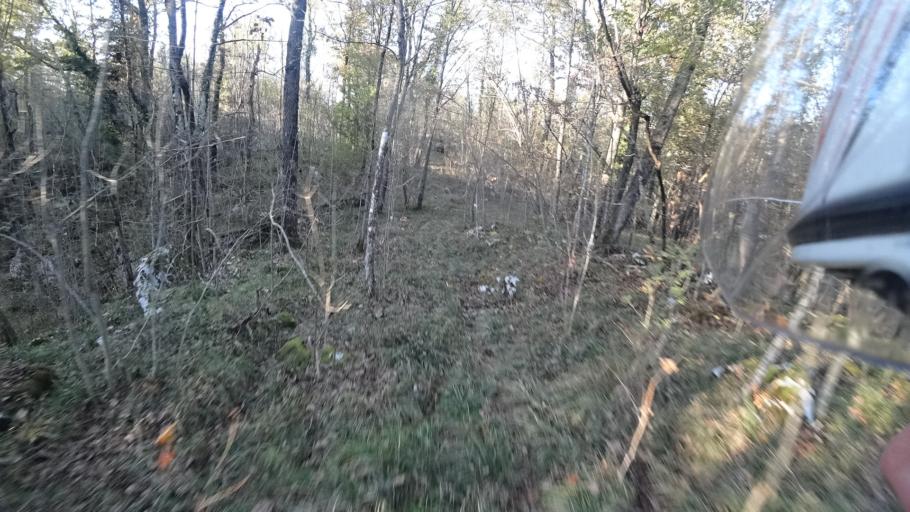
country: HR
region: Primorsko-Goranska
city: Matulji
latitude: 45.4004
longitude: 14.3155
